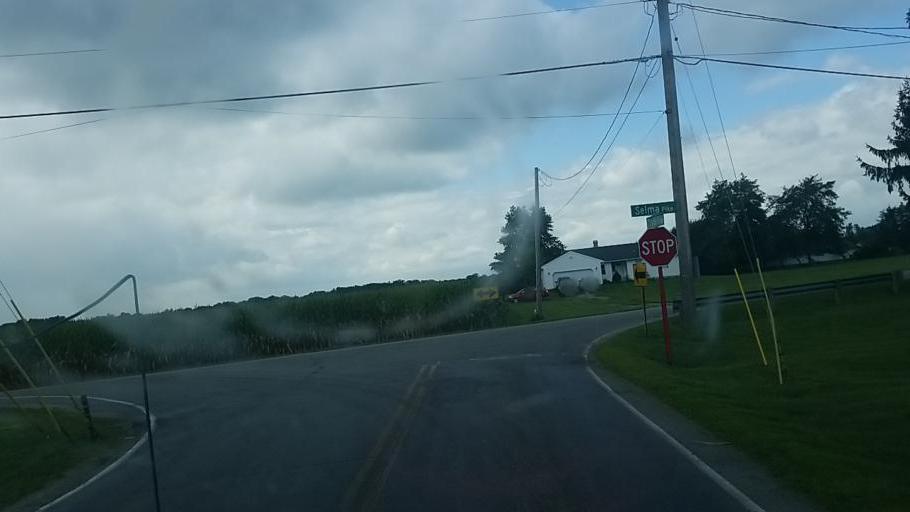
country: US
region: Ohio
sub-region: Clark County
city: Springfield
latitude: 39.8780
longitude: -83.7778
